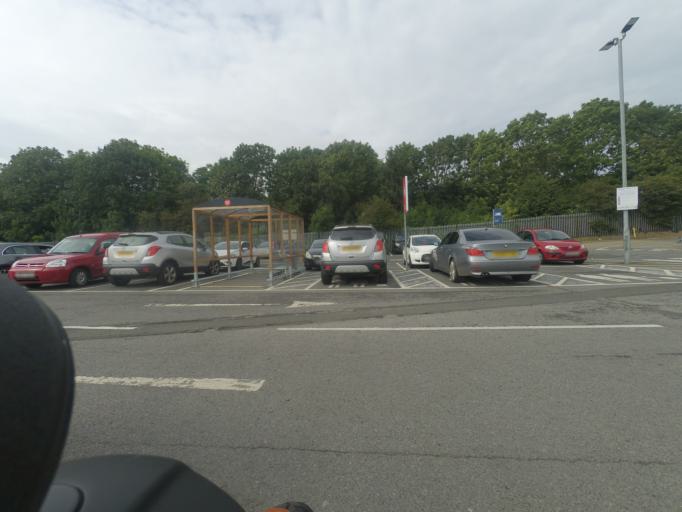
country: GB
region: England
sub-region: South Tyneside
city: Jarrow
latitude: 55.0108
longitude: -1.4866
